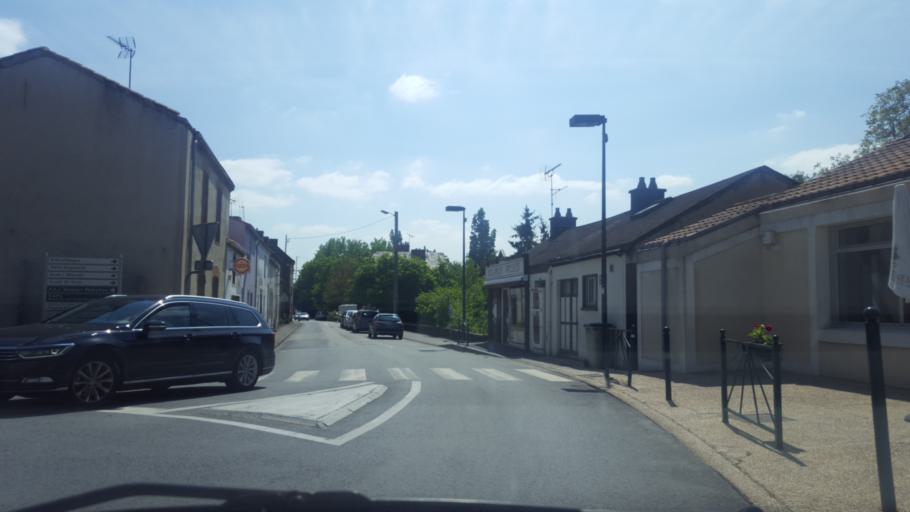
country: FR
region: Pays de la Loire
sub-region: Departement de la Loire-Atlantique
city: La Limouziniere
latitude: 46.9656
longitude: -1.5773
